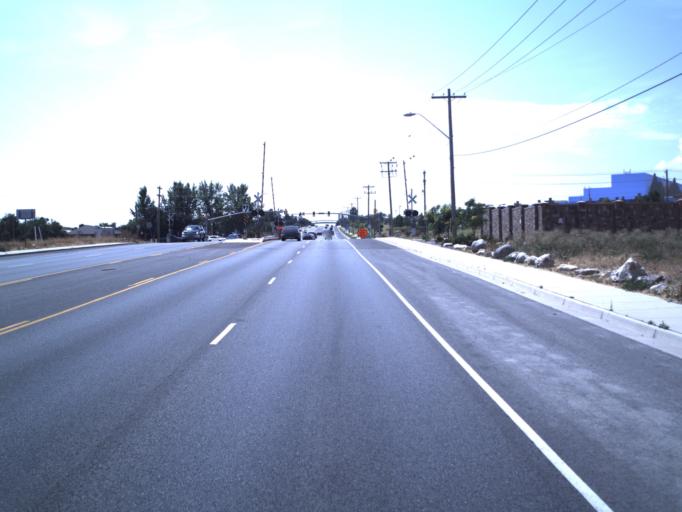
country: US
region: Utah
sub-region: Salt Lake County
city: Kearns
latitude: 40.6695
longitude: -112.0248
